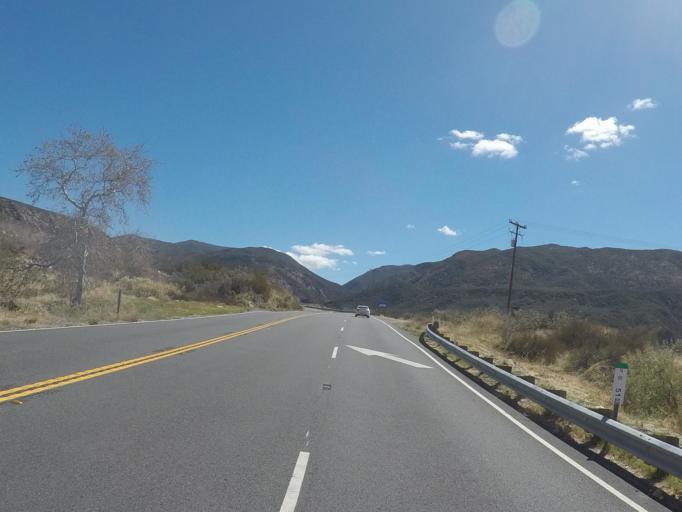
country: US
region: California
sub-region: Riverside County
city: Idyllwild-Pine Cove
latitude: 33.7201
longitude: -116.7941
